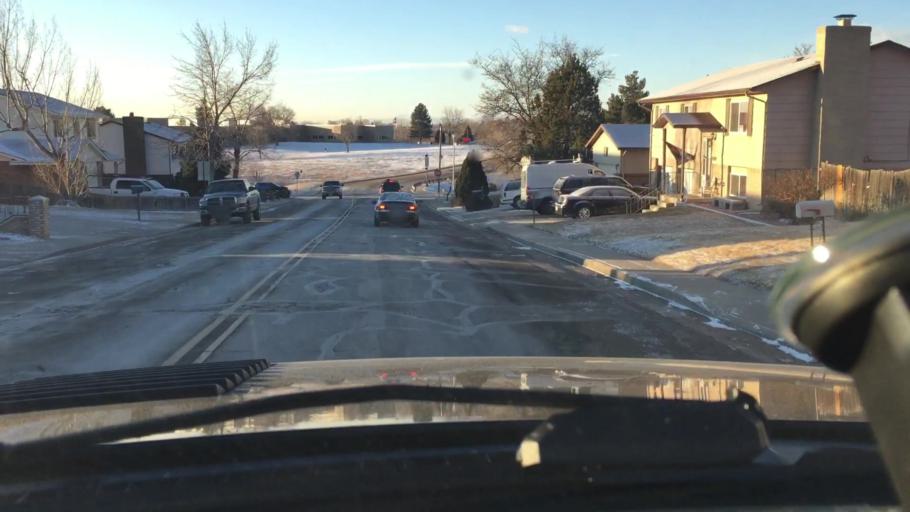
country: US
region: Colorado
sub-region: Adams County
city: Federal Heights
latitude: 39.8718
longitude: -105.0056
